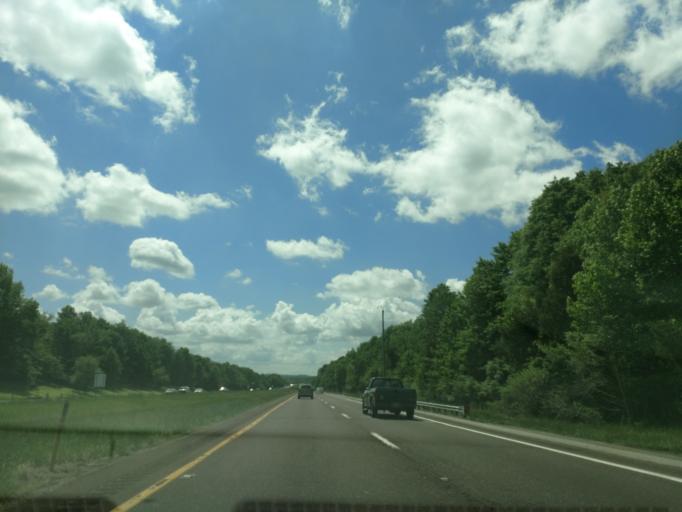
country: US
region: Pennsylvania
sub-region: Montgomery County
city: Audubon
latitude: 40.1161
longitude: -75.4300
